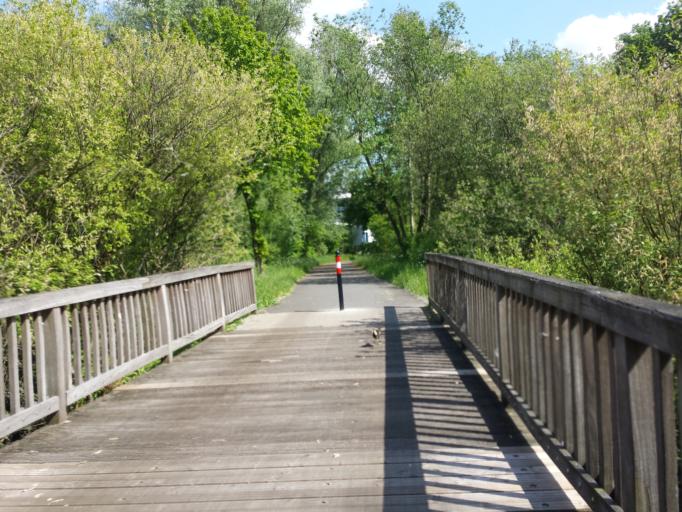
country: DE
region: Lower Saxony
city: Lilienthal
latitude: 53.1131
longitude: 8.8761
